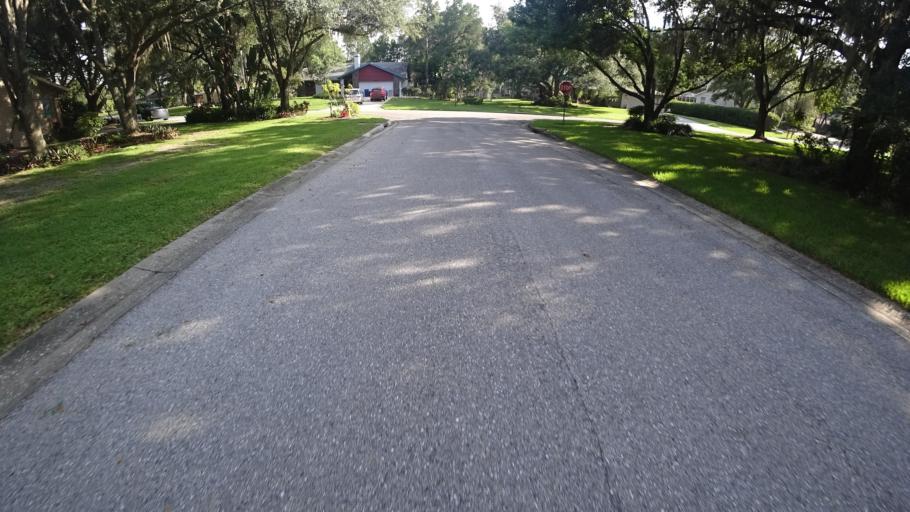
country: US
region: Florida
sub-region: Sarasota County
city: Desoto Lakes
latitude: 27.4300
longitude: -82.4525
